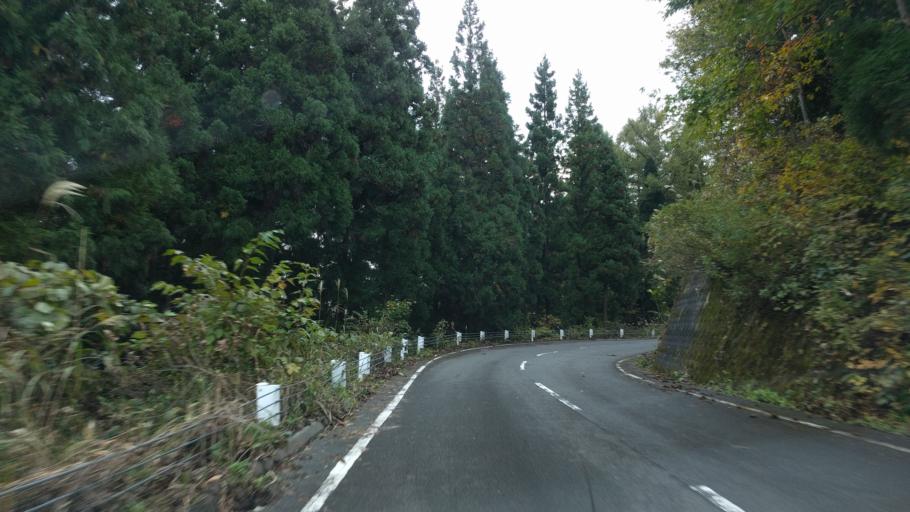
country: JP
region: Fukushima
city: Kitakata
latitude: 37.4256
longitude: 139.7832
